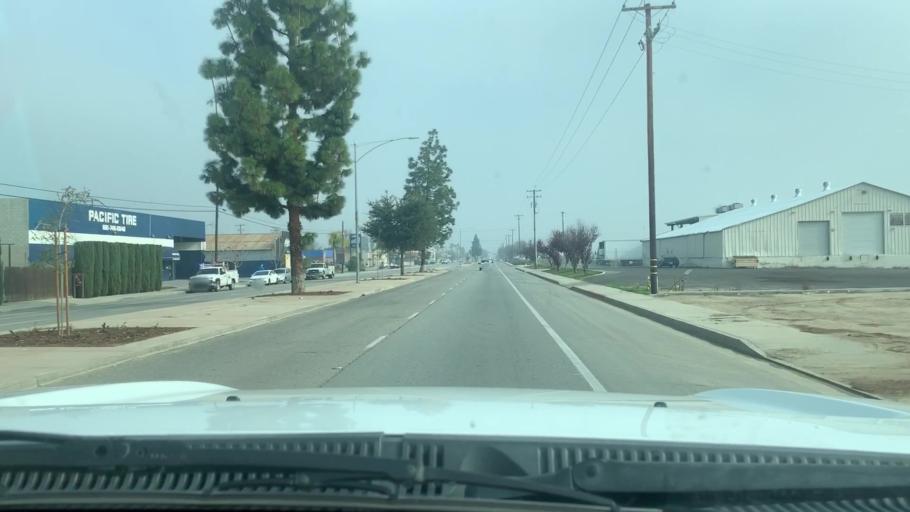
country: US
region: California
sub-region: Kern County
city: Shafter
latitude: 35.4998
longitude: -119.2669
